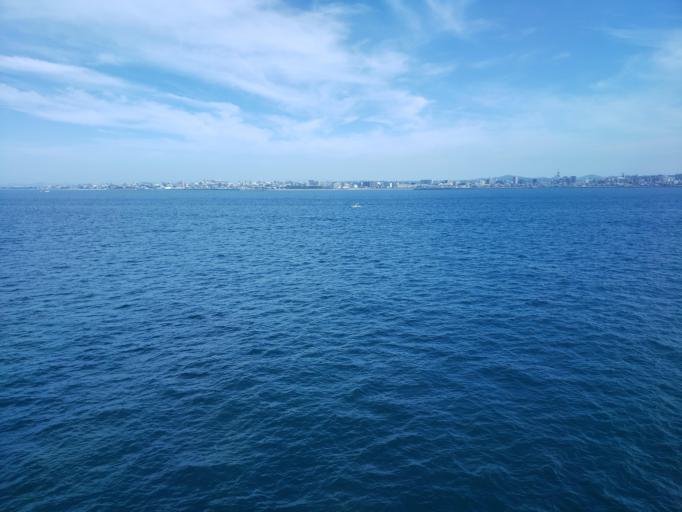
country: JP
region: Hyogo
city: Akashi
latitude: 34.6247
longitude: 134.9806
